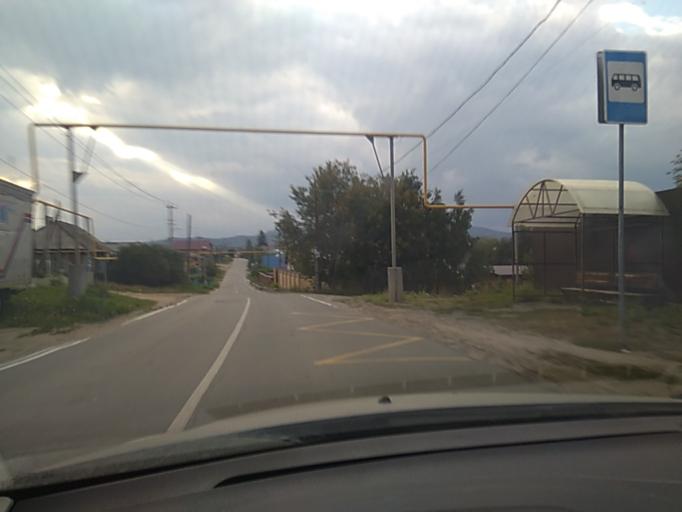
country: RU
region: Chelyabinsk
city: Kyshtym
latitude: 55.6983
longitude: 60.5391
